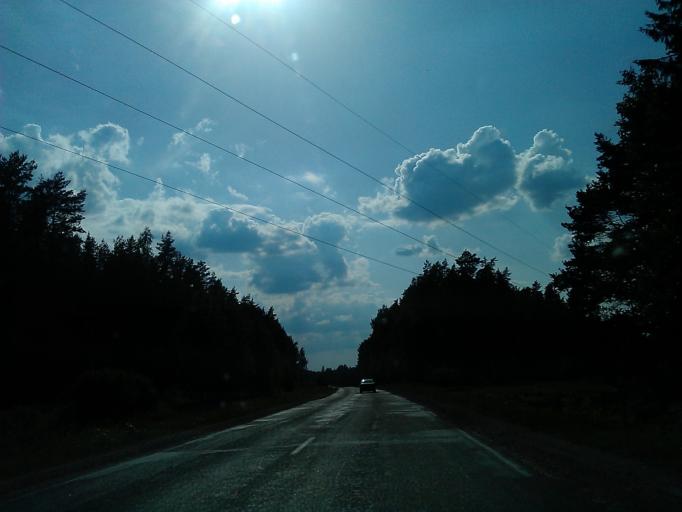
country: LV
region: Skrunda
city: Skrunda
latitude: 56.6806
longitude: 22.0896
